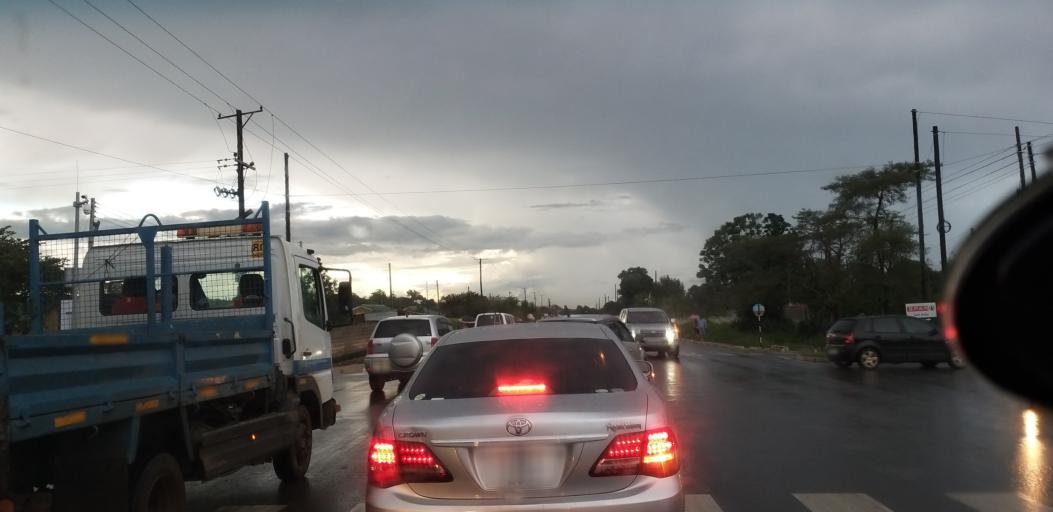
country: ZM
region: Lusaka
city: Lusaka
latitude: -15.4278
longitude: 28.3560
